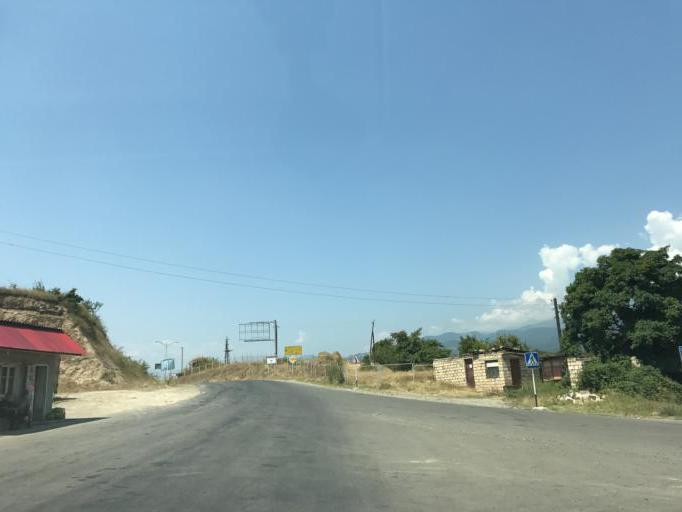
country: AZ
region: Tartar Rayon
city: Martakert
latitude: 40.1463
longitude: 46.6026
